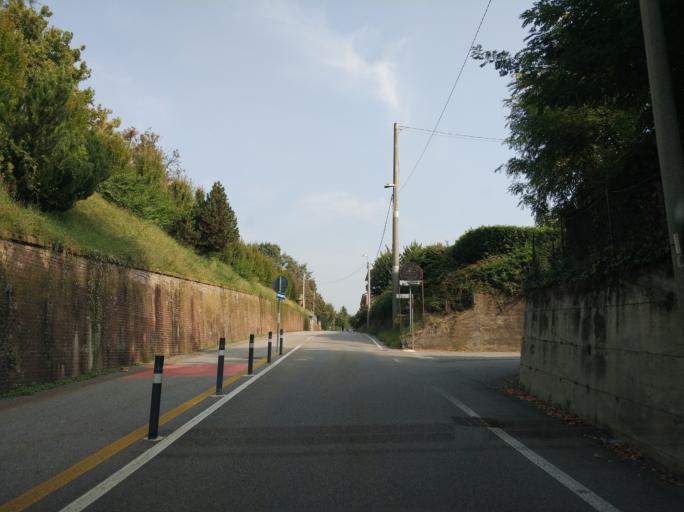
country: IT
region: Piedmont
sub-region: Provincia di Torino
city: San Carlo Canavese
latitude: 45.2439
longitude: 7.6083
